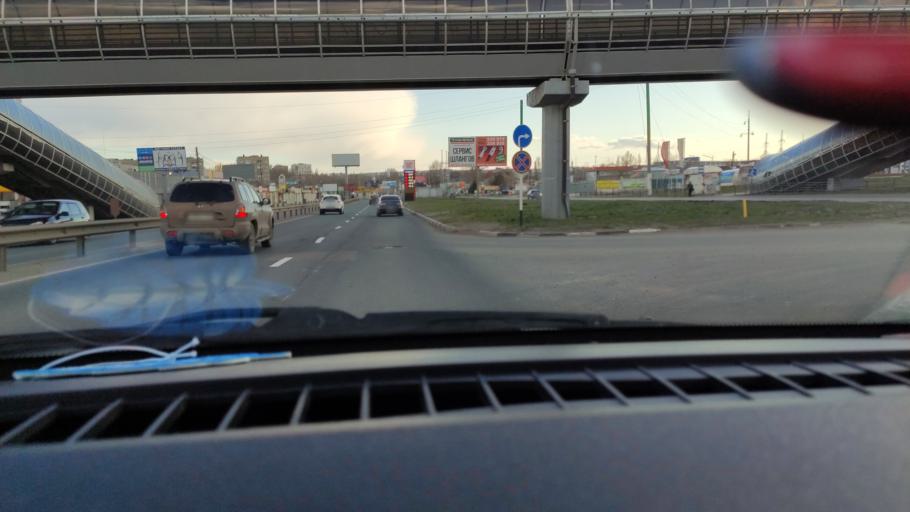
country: RU
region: Saratov
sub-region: Saratovskiy Rayon
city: Saratov
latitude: 51.6162
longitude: 45.9719
